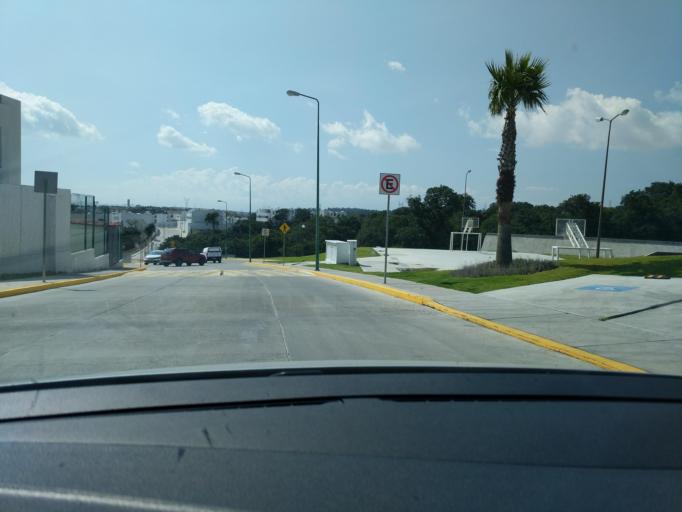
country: MX
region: Puebla
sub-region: Puebla
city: Galaxia la Calera
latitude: 19.0079
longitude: -98.1407
